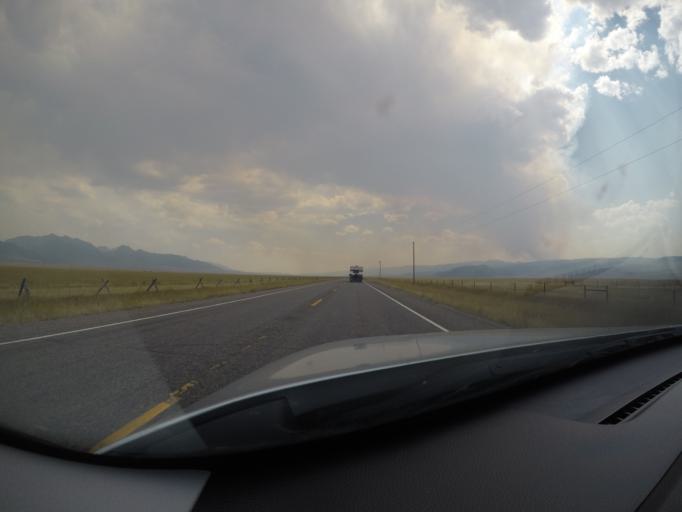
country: US
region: Montana
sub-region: Madison County
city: Virginia City
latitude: 45.1582
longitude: -111.6786
